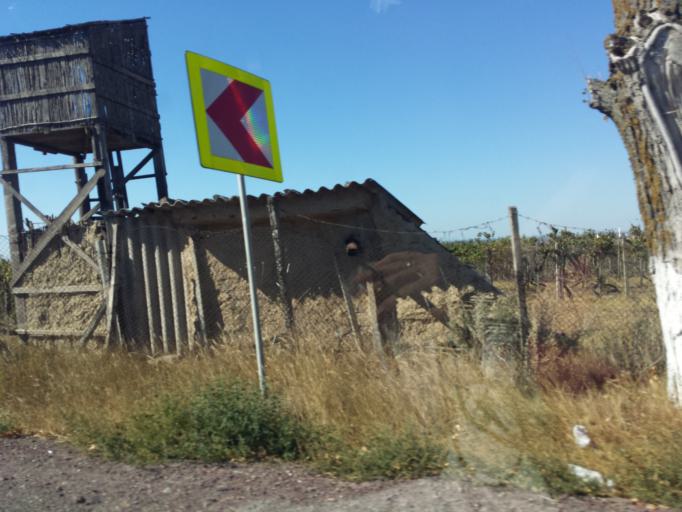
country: RO
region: Tulcea
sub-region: Municipiul Tulcea
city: Tulcea
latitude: 45.1404
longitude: 28.7736
